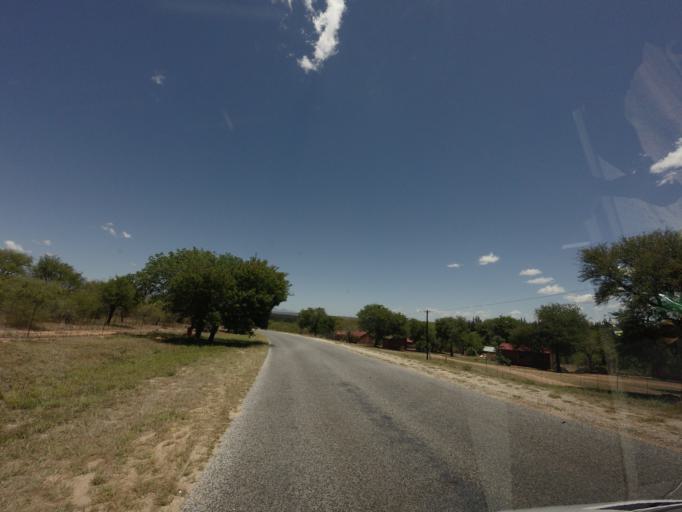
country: ZA
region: Limpopo
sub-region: Mopani District Municipality
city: Hoedspruit
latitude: -24.3714
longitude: 30.7289
